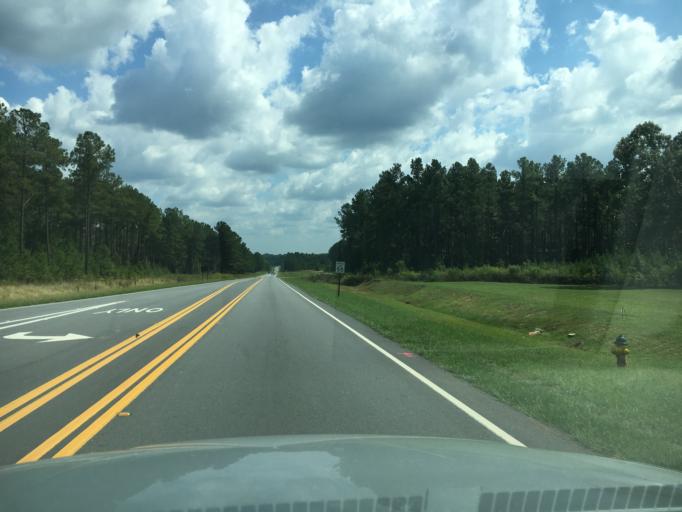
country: US
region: South Carolina
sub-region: Greenwood County
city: Greenwood
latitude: 34.1573
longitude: -82.1738
